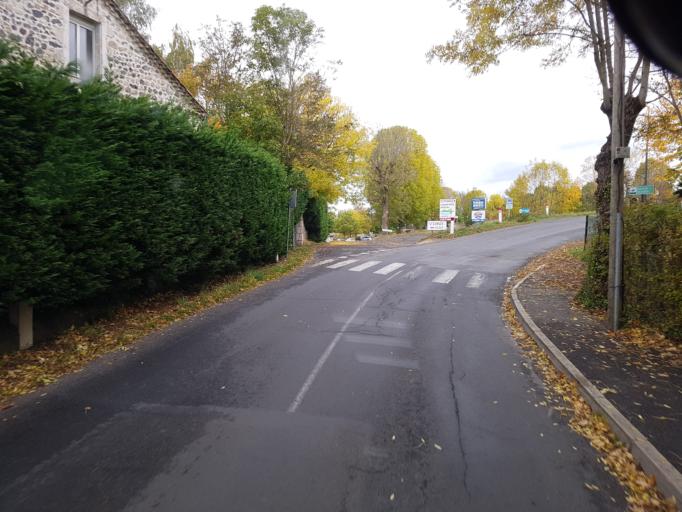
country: FR
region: Languedoc-Roussillon
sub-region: Departement de la Lozere
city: Langogne
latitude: 44.7247
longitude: 3.8398
